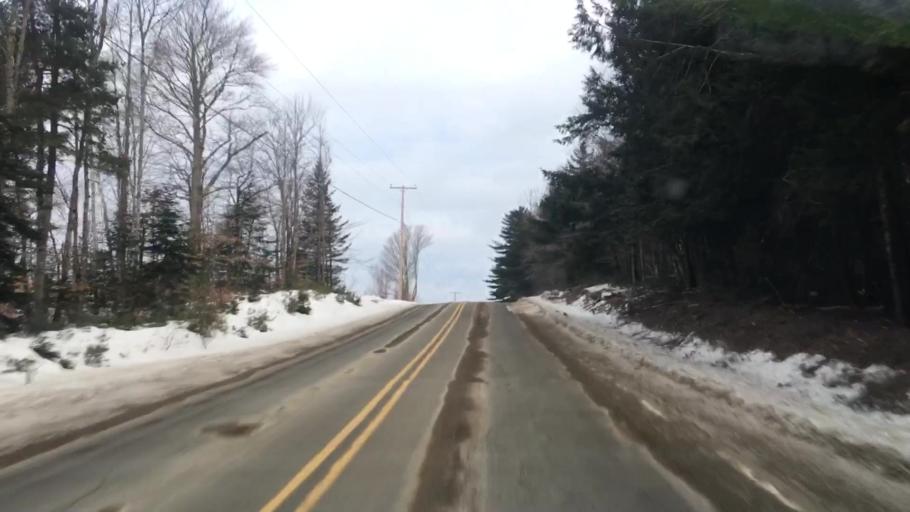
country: US
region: Maine
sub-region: Hancock County
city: Franklin
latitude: 44.8425
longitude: -68.3257
